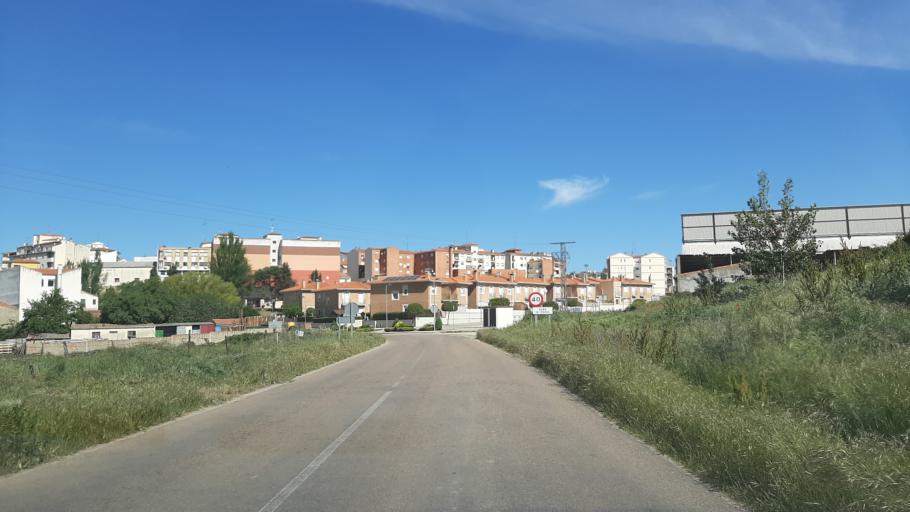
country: ES
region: Castille and Leon
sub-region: Provincia de Salamanca
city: Alba de Tormes
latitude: 40.8233
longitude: -5.5071
